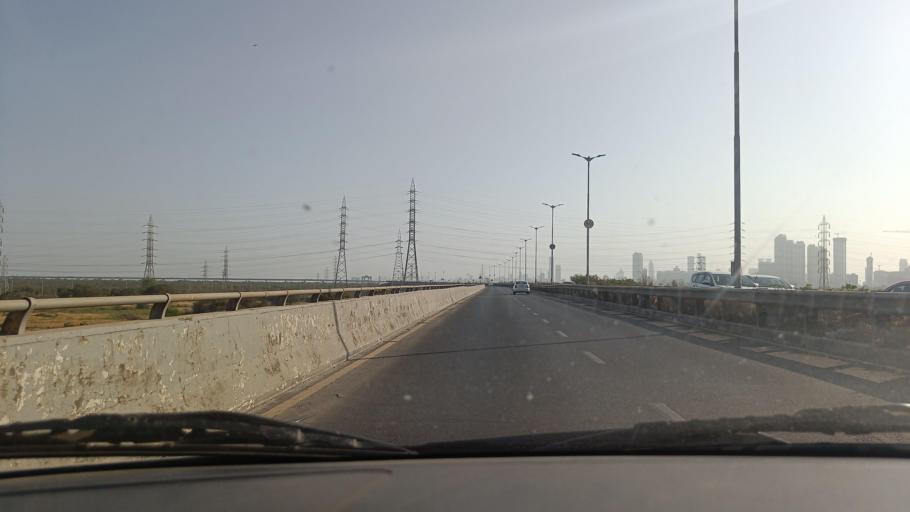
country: IN
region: Maharashtra
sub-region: Mumbai Suburban
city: Mumbai
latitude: 19.0190
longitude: 72.8741
